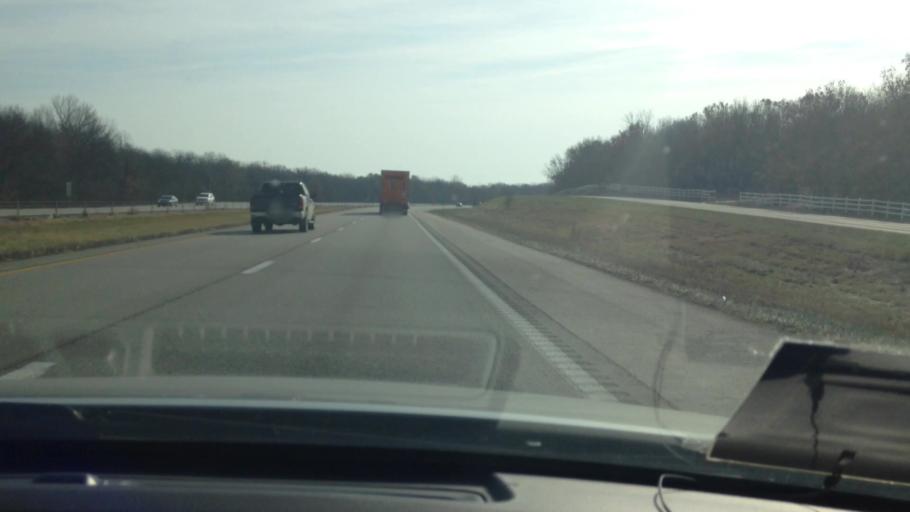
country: US
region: Missouri
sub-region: Cass County
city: Peculiar
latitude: 38.7592
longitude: -94.4854
